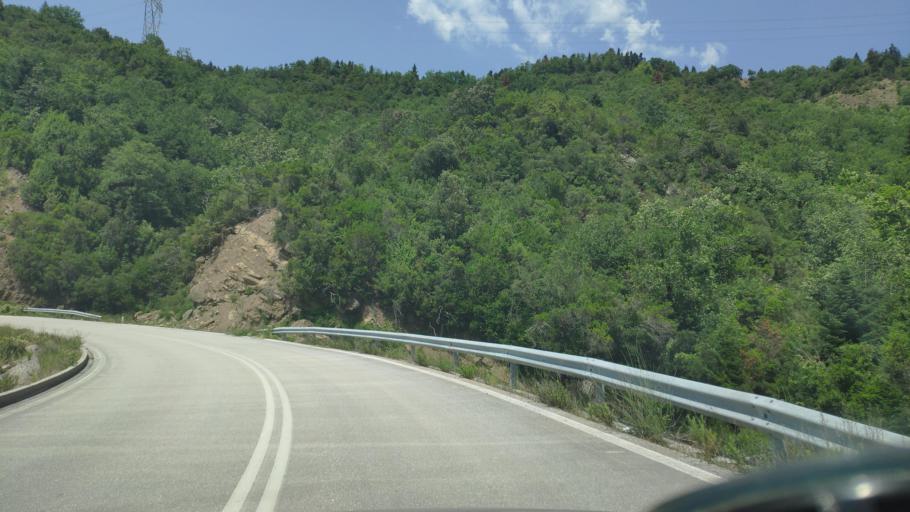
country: GR
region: Thessaly
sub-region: Nomos Kardhitsas
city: Anthiro
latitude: 39.2737
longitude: 21.3310
